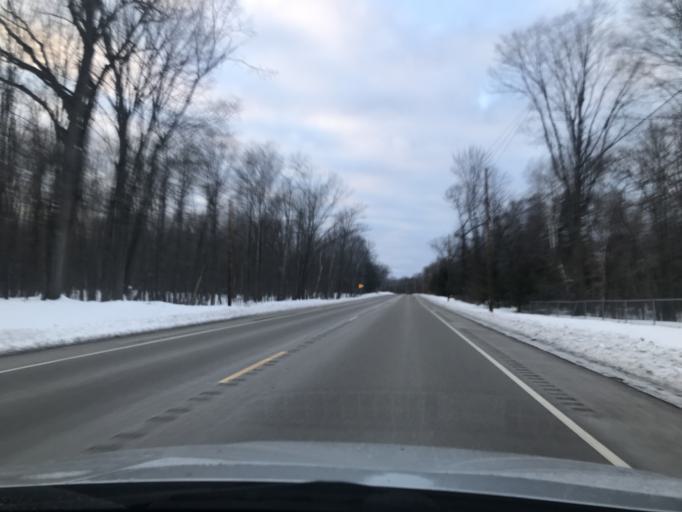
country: US
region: Wisconsin
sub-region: Marinette County
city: Marinette
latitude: 45.1499
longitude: -87.7034
